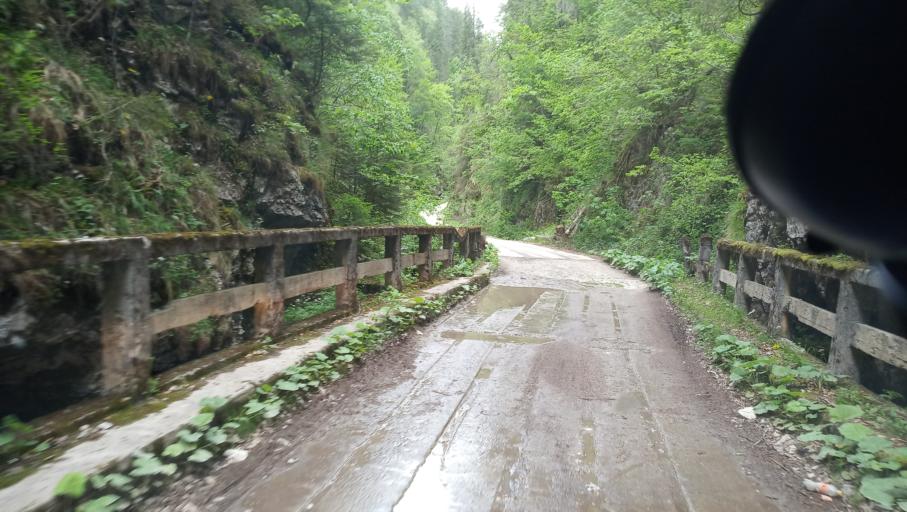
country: RO
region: Alba
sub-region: Comuna Scarisoara
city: Scarisoara
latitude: 46.4690
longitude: 22.8452
